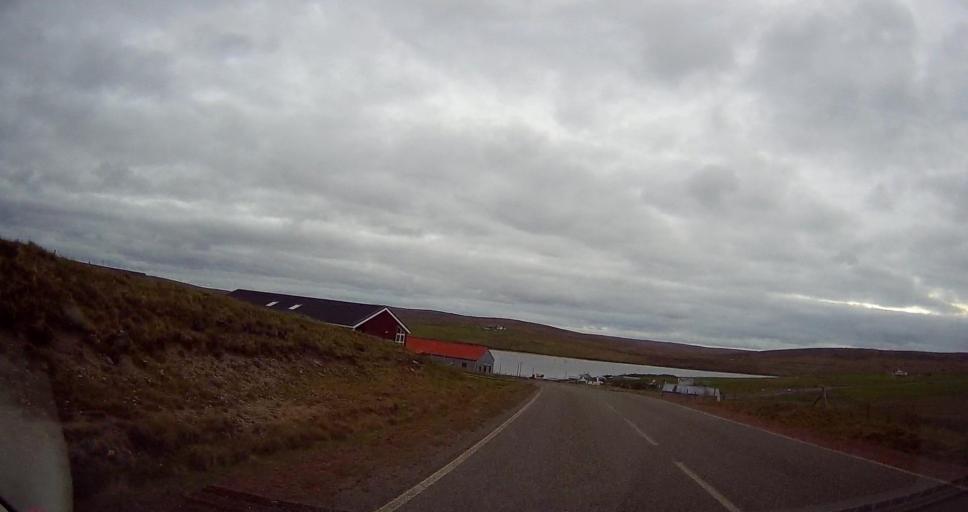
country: GB
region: Scotland
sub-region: Shetland Islands
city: Shetland
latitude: 60.6625
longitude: -1.0432
